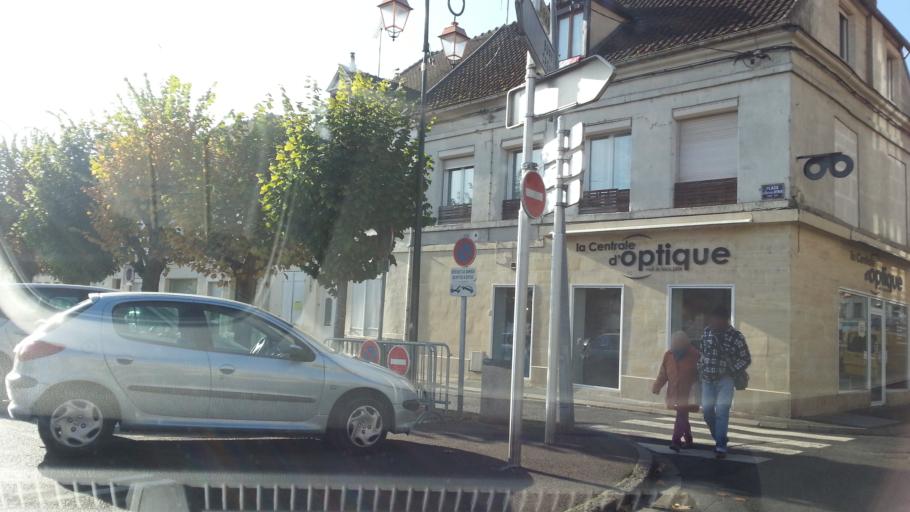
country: FR
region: Picardie
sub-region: Departement de l'Oise
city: Mouy
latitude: 49.3198
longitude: 2.3204
